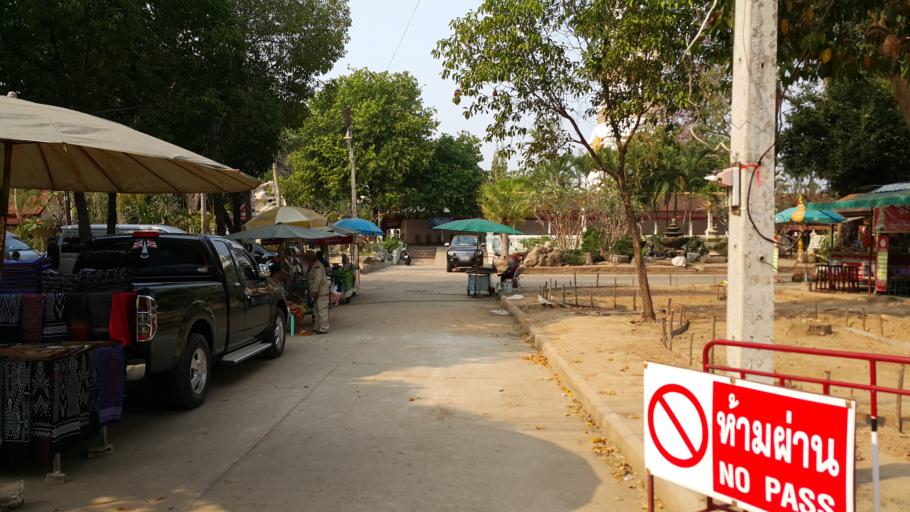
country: TH
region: Nakhon Phanom
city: That Phanom
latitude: 16.9417
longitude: 104.7236
